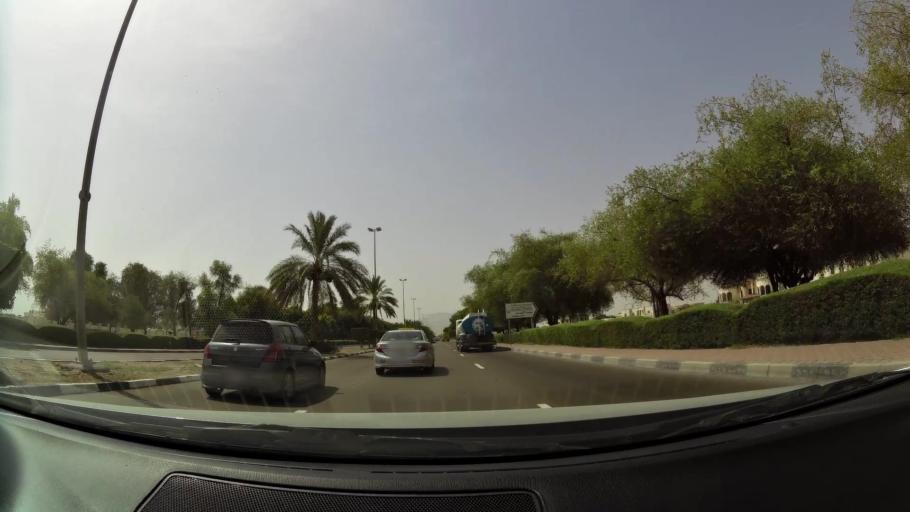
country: AE
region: Abu Dhabi
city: Al Ain
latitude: 24.1776
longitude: 55.7052
